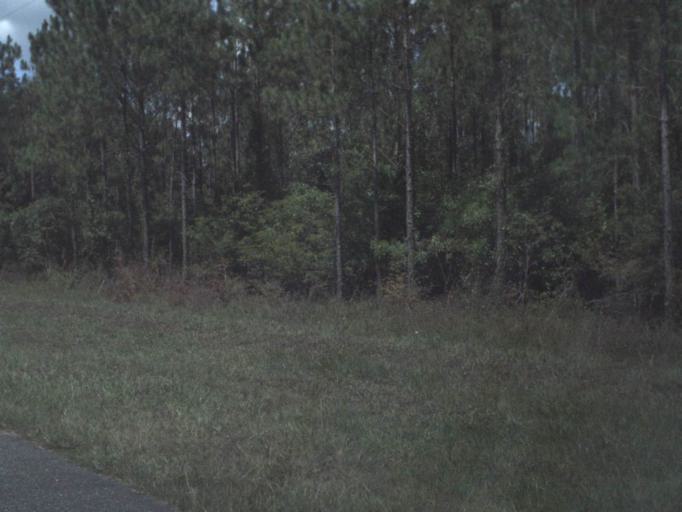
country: US
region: Florida
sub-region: Alachua County
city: High Springs
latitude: 29.7604
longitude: -82.7406
